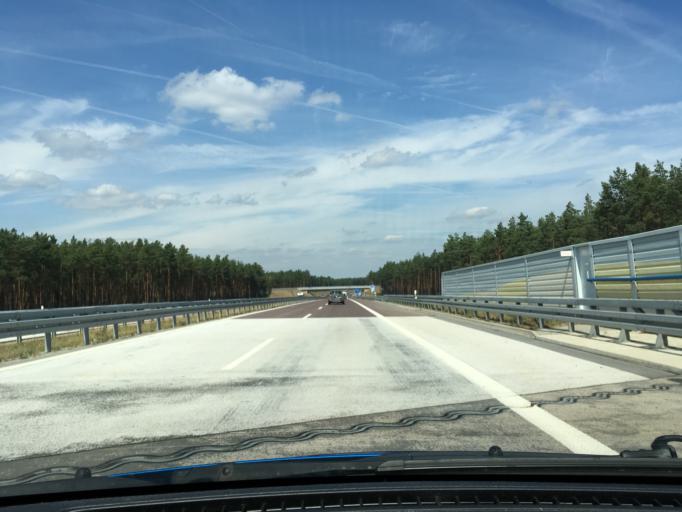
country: DE
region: Mecklenburg-Vorpommern
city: Ludwigslust
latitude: 53.3390
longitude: 11.5224
